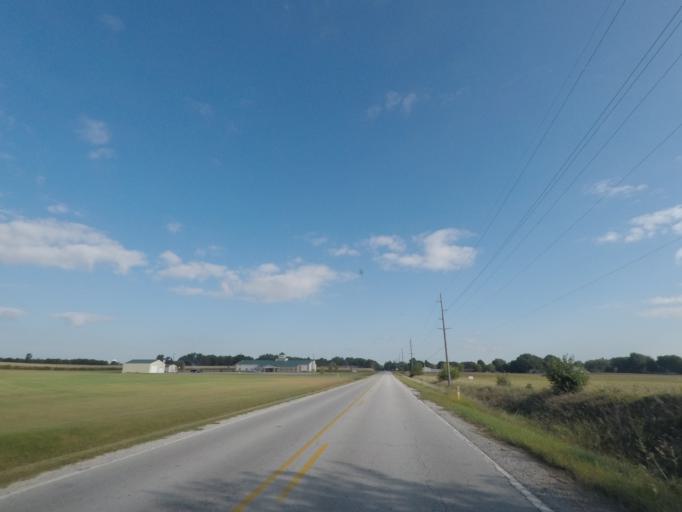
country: US
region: Iowa
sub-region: Story County
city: Nevada
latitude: 42.0111
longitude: -93.4628
